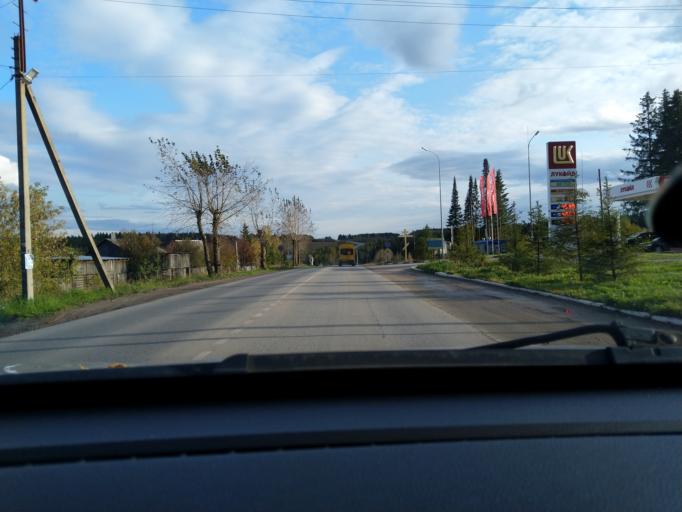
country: RU
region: Perm
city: Polazna
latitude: 58.2833
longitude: 56.4113
